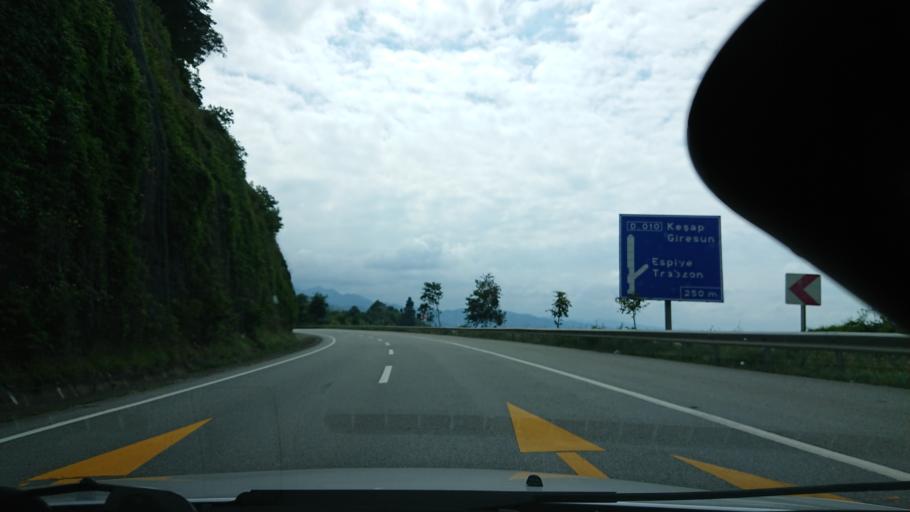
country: TR
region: Giresun
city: Kesap
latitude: 40.9427
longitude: 38.5799
